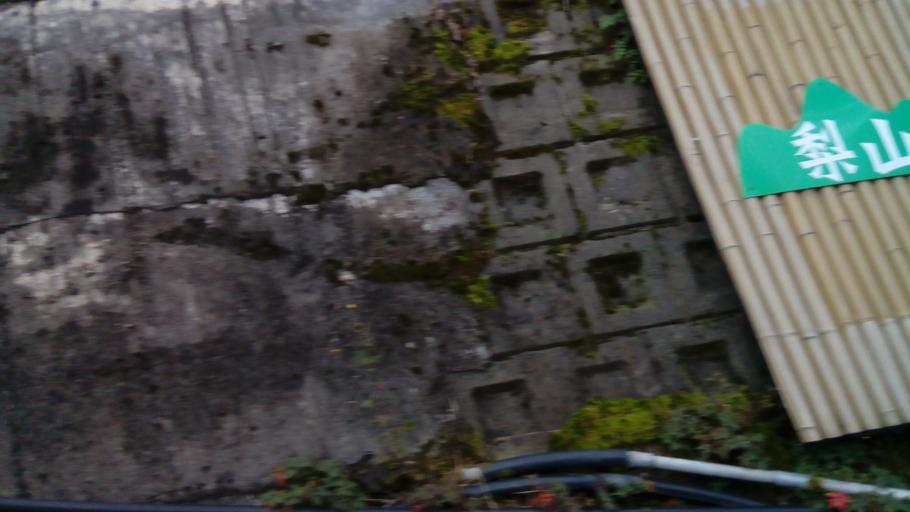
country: TW
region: Taiwan
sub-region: Nantou
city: Puli
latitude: 24.2541
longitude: 121.2479
